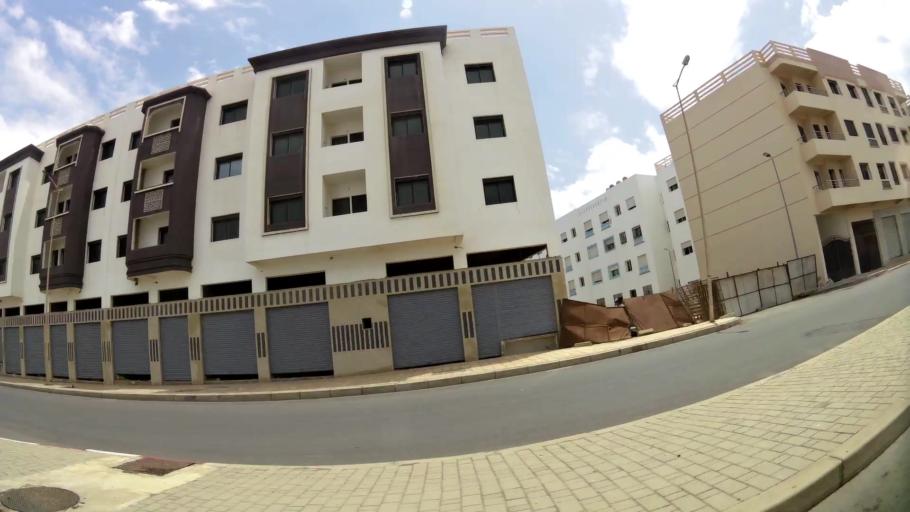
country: MA
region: Rabat-Sale-Zemmour-Zaer
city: Sale
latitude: 34.0614
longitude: -6.8125
